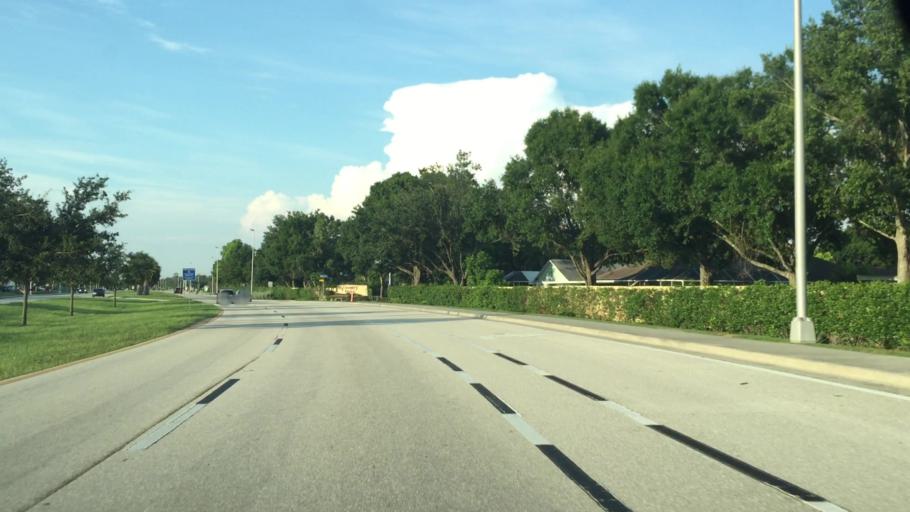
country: US
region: Florida
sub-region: Lee County
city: Three Oaks
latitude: 26.4562
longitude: -81.7888
